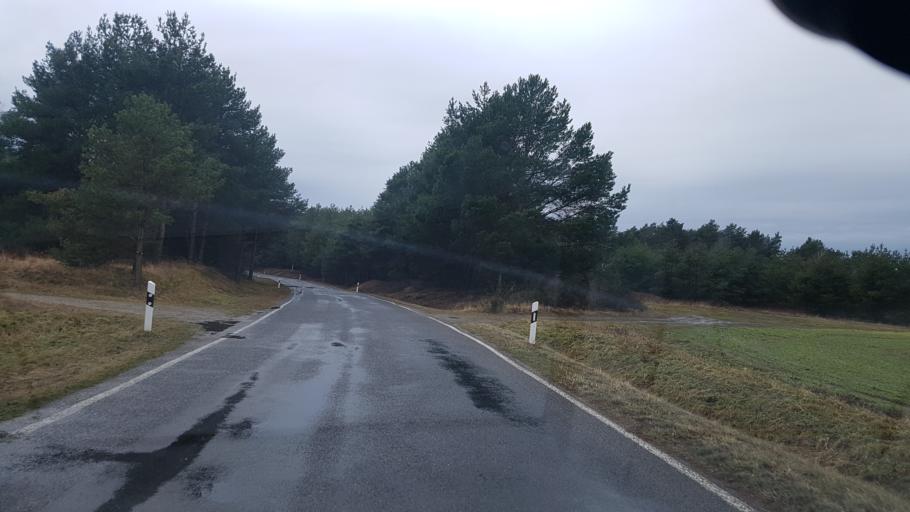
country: DE
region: Brandenburg
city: Neupetershain
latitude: 51.6262
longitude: 14.1177
